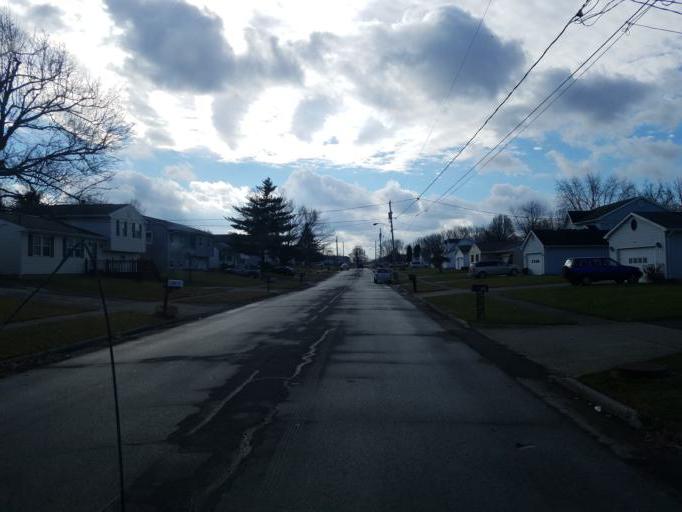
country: US
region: Ohio
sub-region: Marion County
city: Marion
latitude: 40.5710
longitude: -83.1544
